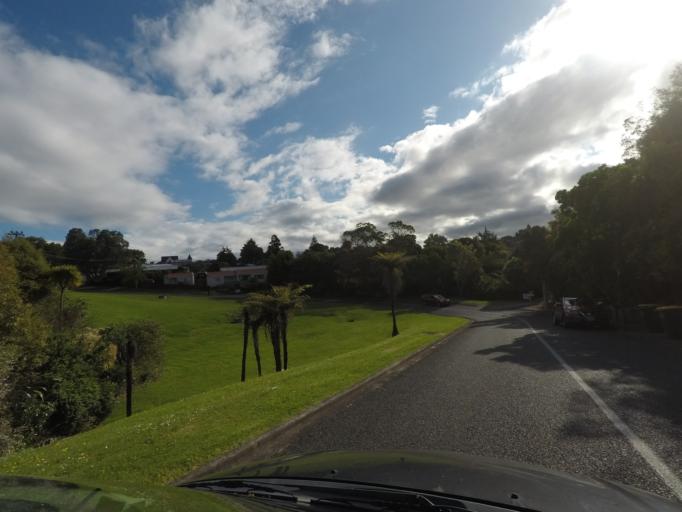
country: NZ
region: Auckland
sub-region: Auckland
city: Rosebank
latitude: -36.8818
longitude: 174.6523
